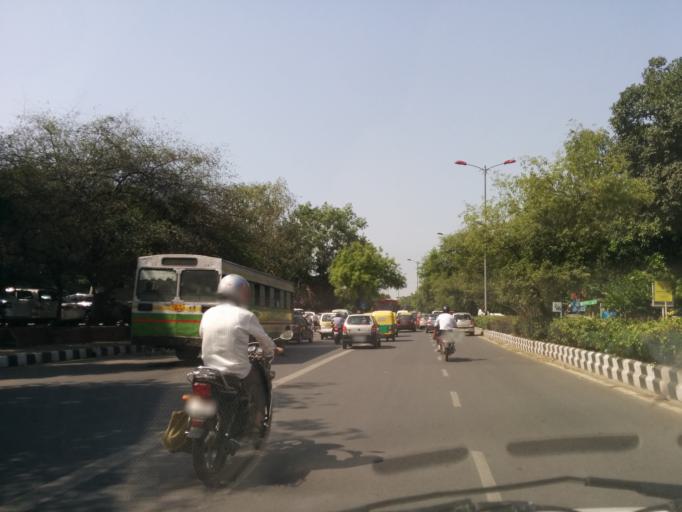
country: IN
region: NCT
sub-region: New Delhi
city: New Delhi
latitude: 28.5534
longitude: 77.2052
